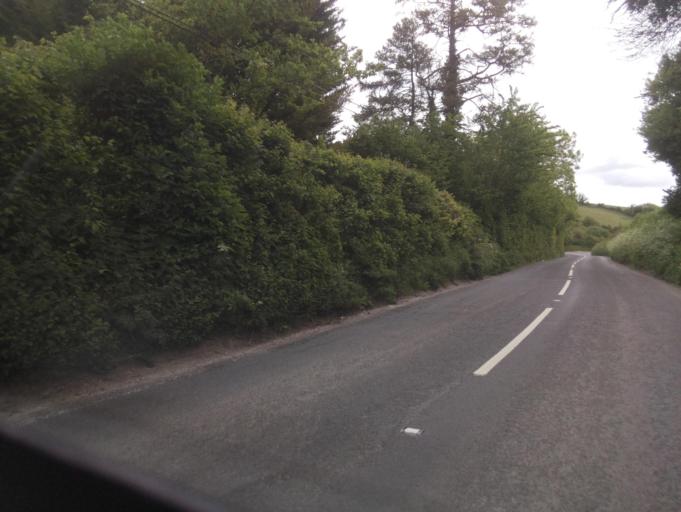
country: GB
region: England
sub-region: Dorset
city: Dorchester
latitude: 50.7475
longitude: -2.4635
